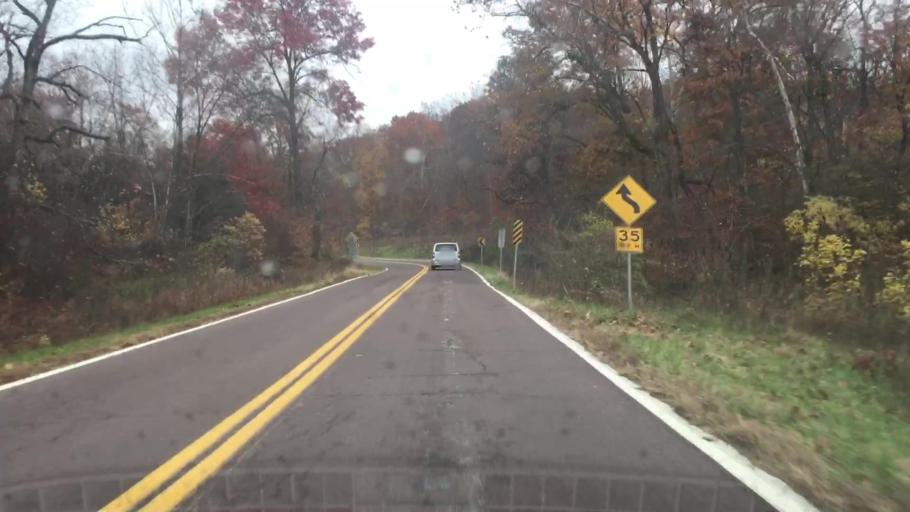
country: US
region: Missouri
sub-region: Callaway County
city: Fulton
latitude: 38.7891
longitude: -91.7523
